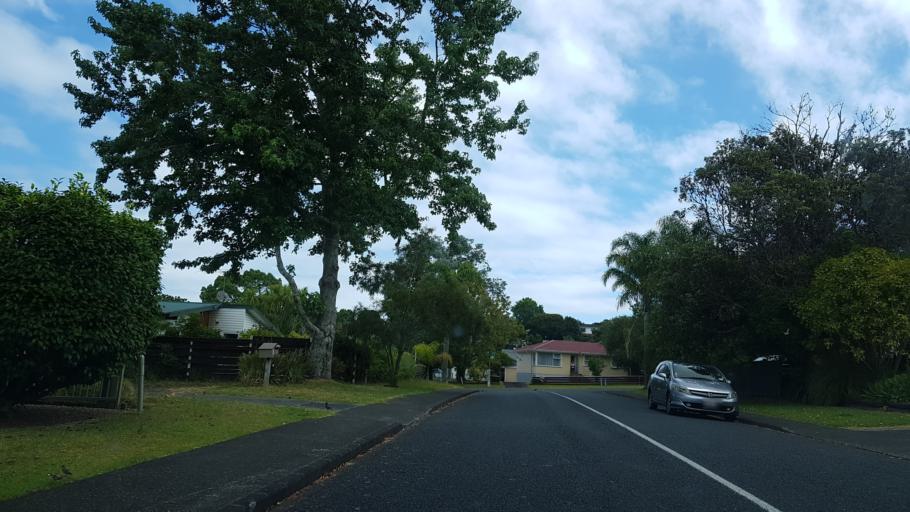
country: NZ
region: Auckland
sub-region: Auckland
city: North Shore
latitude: -36.7747
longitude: 174.7285
